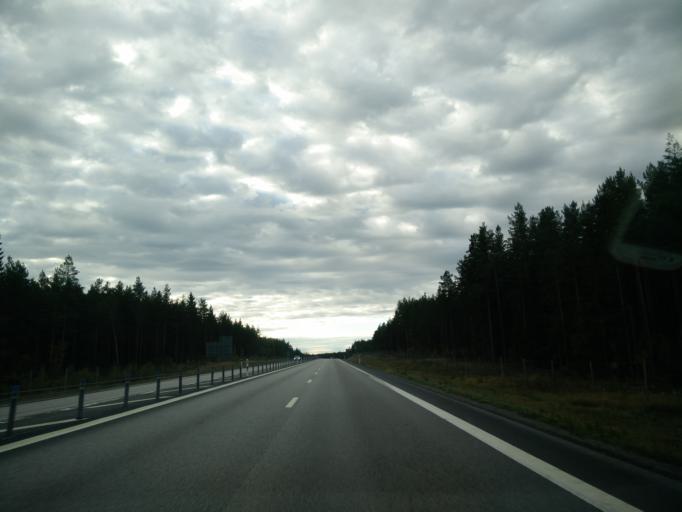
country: SE
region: Gaevleborg
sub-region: Hudiksvalls Kommun
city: Hudiksvall
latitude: 61.7069
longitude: 17.0504
